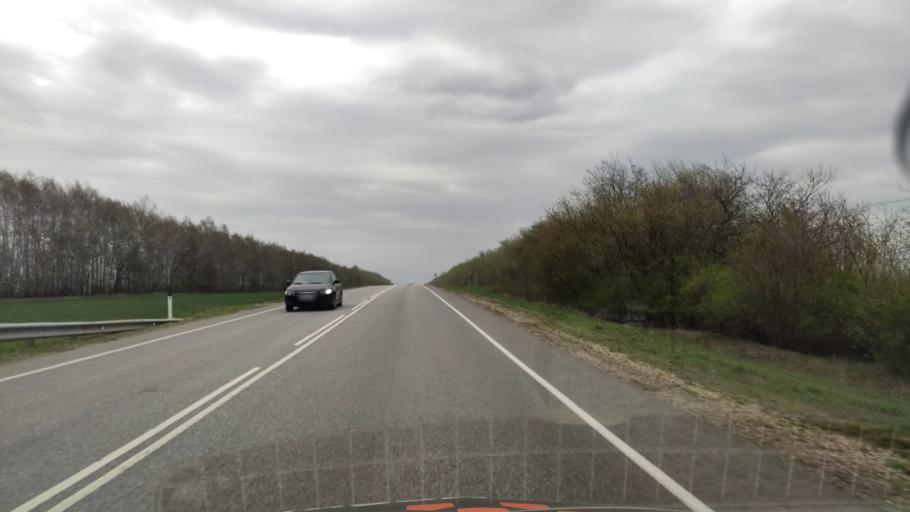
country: RU
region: Kursk
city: Gorshechnoye
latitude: 51.5493
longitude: 38.1509
